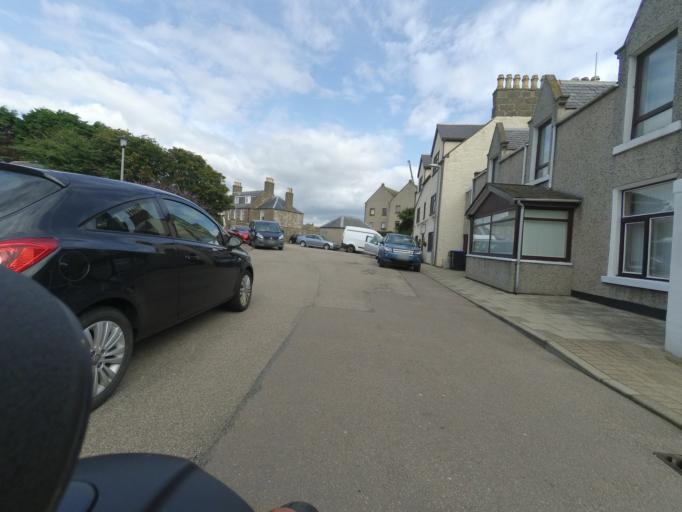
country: GB
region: Scotland
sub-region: Aberdeenshire
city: Stonehaven
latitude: 56.9616
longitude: -2.2070
